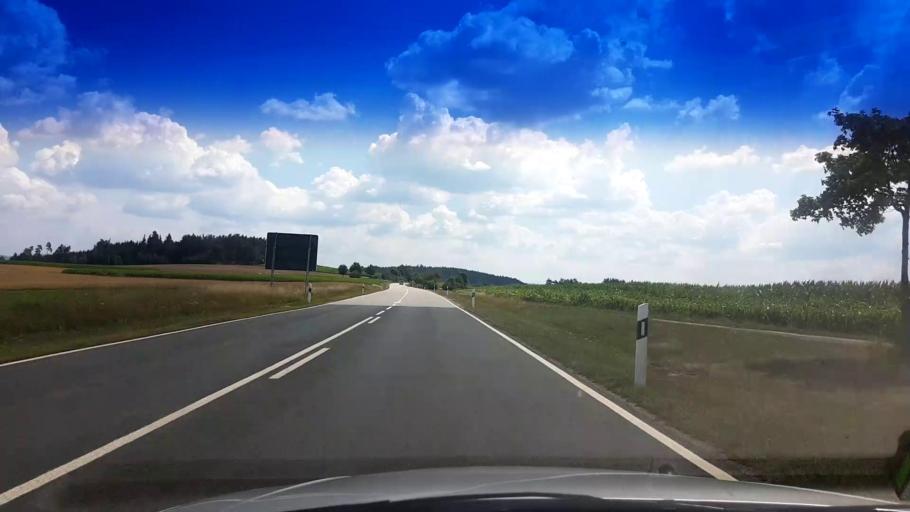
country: DE
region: Bavaria
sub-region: Upper Palatinate
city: Wiesau
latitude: 49.8633
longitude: 12.2385
